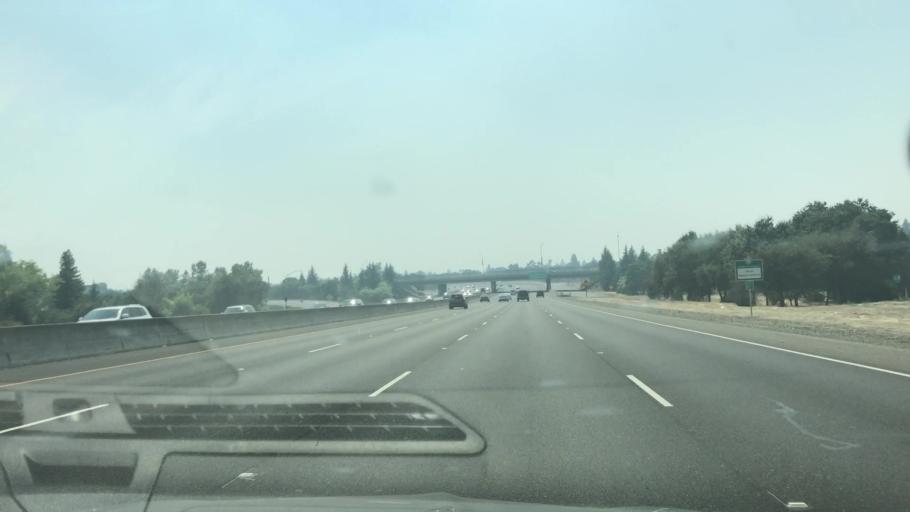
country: US
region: California
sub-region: Sacramento County
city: Gold River
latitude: 38.6109
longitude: -121.2670
